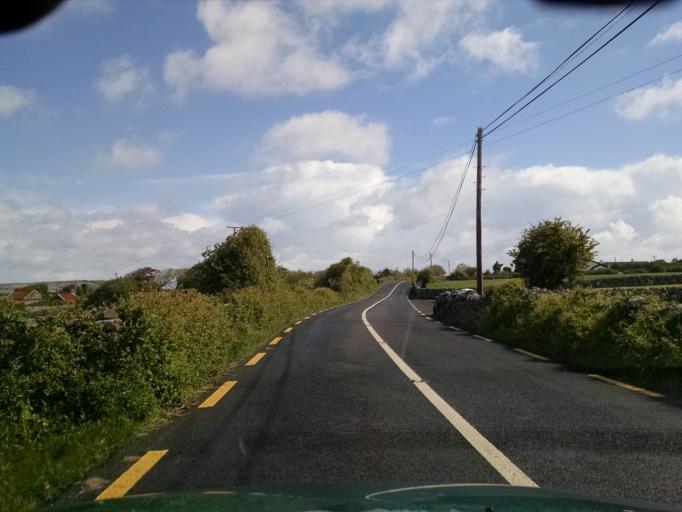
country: IE
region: Connaught
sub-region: County Galway
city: Bearna
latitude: 53.1315
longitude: -9.1177
